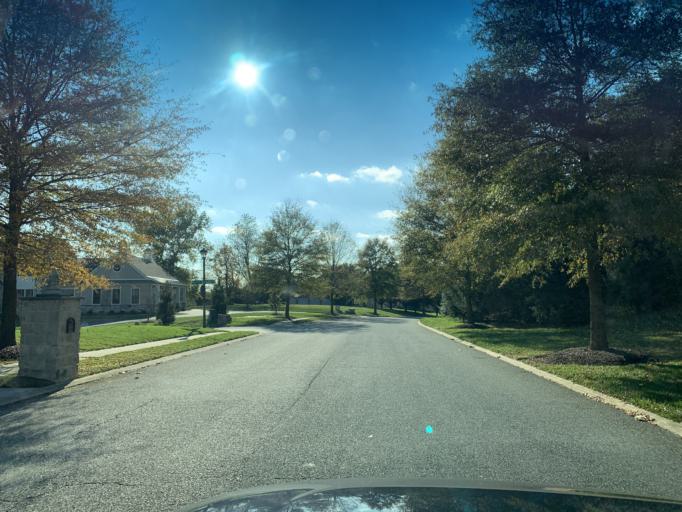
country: US
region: Maryland
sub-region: Harford County
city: Bel Air South
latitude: 39.5127
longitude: -76.3024
